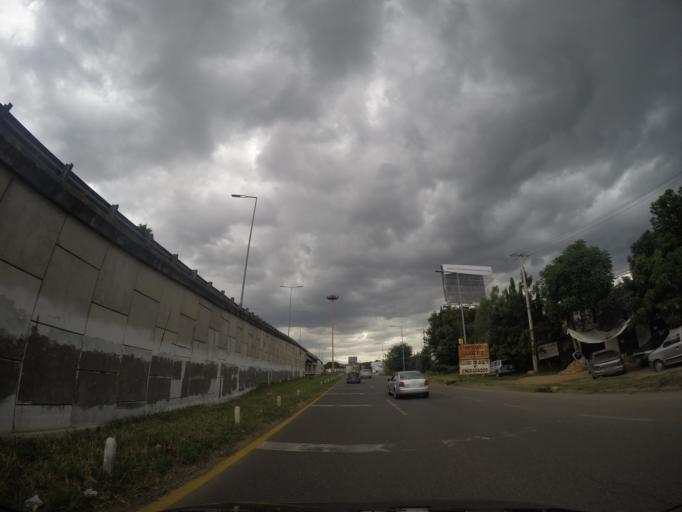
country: MX
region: Oaxaca
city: Tlalixtac de Cabrera
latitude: 17.0596
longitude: -96.6611
